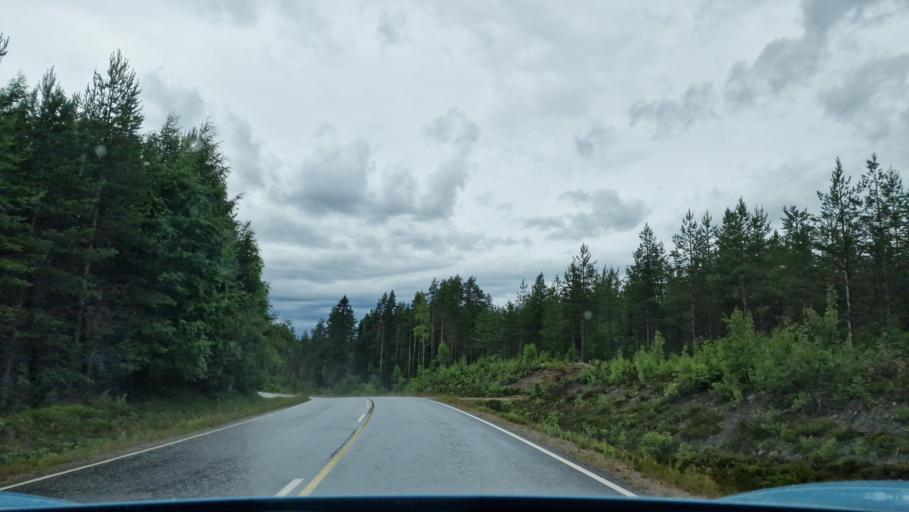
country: FI
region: Central Finland
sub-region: Saarijaervi-Viitasaari
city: Pylkoenmaeki
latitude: 62.6681
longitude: 24.5354
